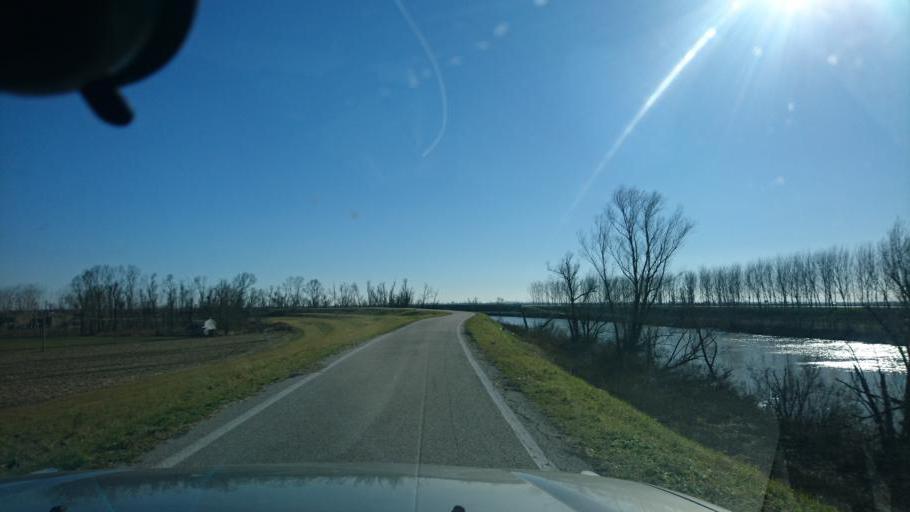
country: IT
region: Veneto
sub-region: Provincia di Rovigo
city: Ariano
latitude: 44.9310
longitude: 12.1383
